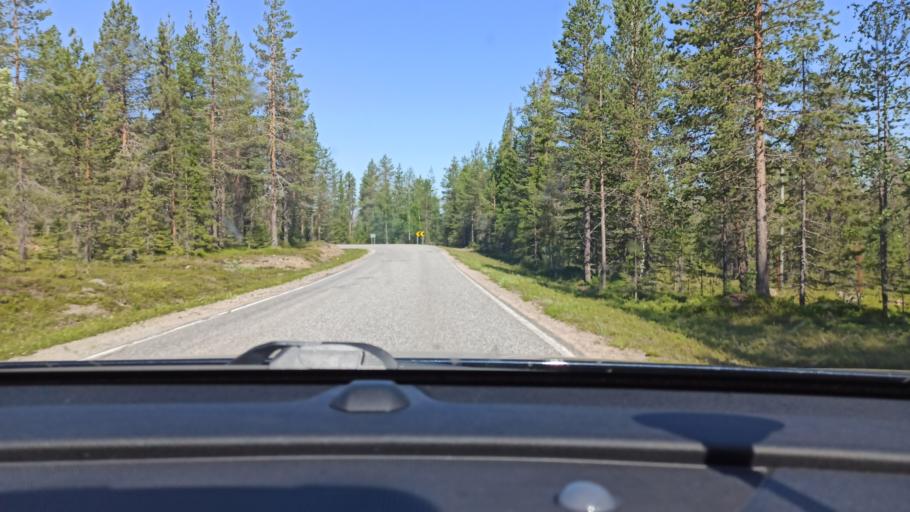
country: FI
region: Lapland
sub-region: Tunturi-Lappi
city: Kolari
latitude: 67.6814
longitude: 24.1374
